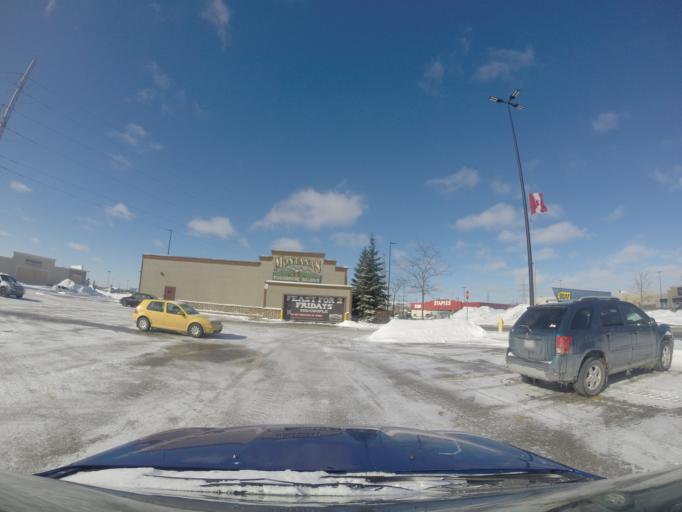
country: CA
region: Ontario
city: Cambridge
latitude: 43.4116
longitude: -80.3238
